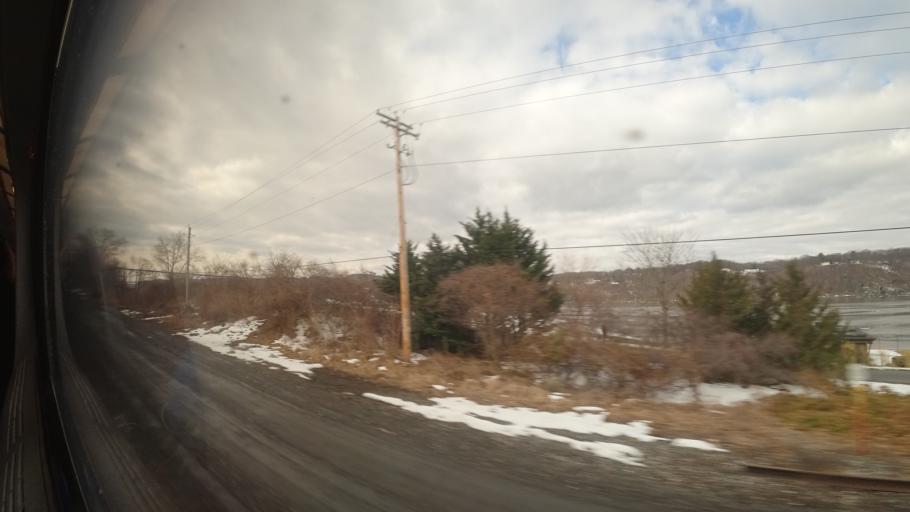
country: US
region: New York
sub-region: Dutchess County
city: Fairview
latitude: 41.7223
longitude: -73.9373
